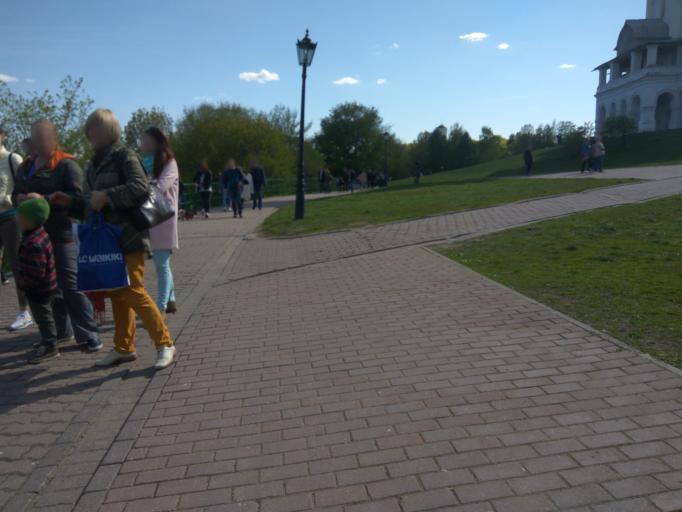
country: RU
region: Moscow
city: Kolomenskoye
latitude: 55.6678
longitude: 37.6718
